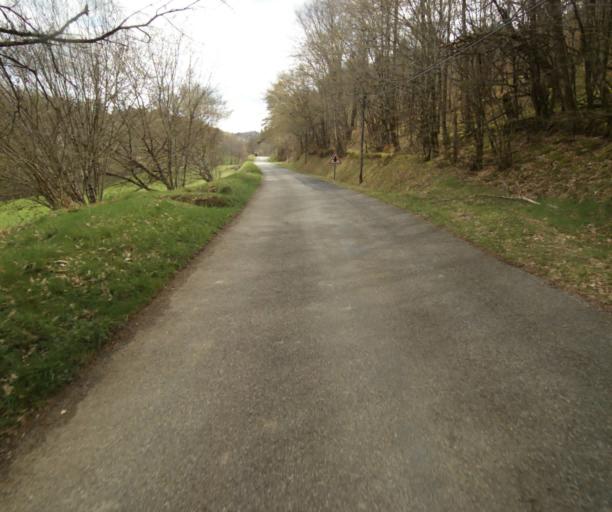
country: FR
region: Limousin
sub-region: Departement de la Correze
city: Laguenne
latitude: 45.2326
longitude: 1.8525
